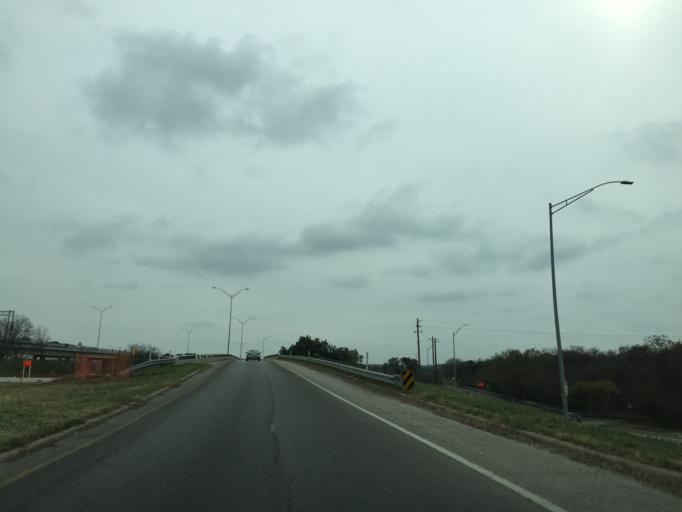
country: US
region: Texas
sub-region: Travis County
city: Rollingwood
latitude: 30.2802
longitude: -97.7685
